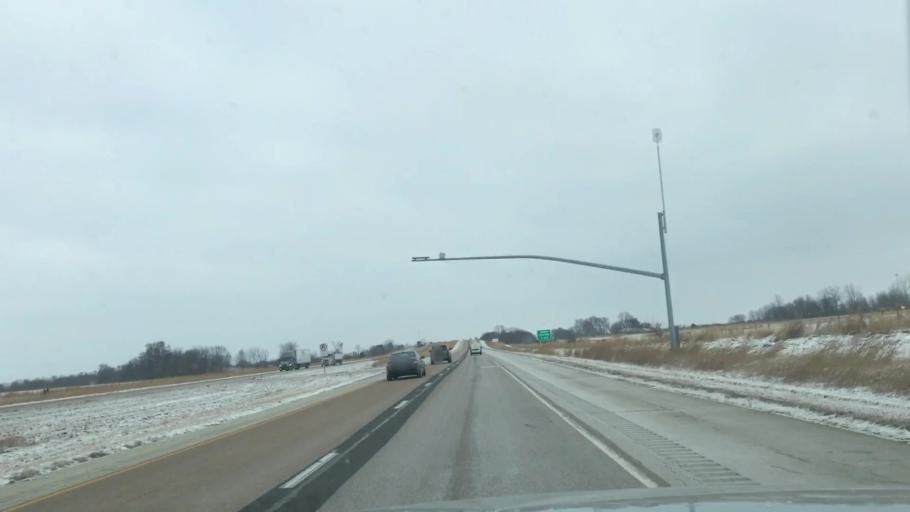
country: US
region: Illinois
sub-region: Montgomery County
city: Litchfield
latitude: 39.2084
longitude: -89.6565
